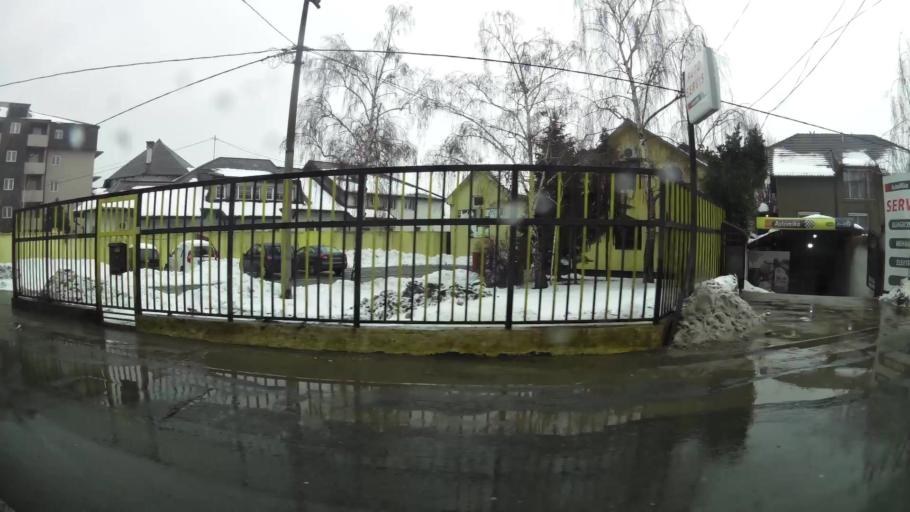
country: RS
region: Central Serbia
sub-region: Belgrade
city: Zemun
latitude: 44.8485
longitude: 20.3696
